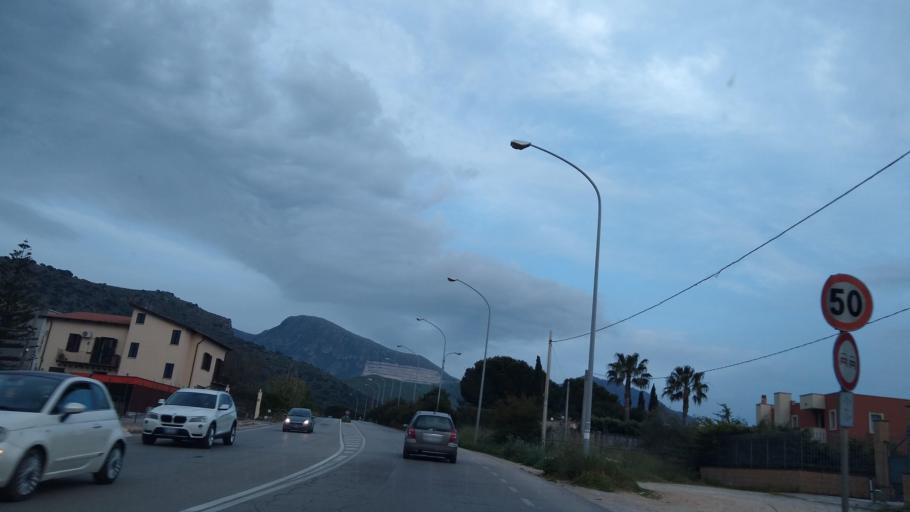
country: IT
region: Sicily
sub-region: Palermo
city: Partinico
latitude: 38.0377
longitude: 13.1096
